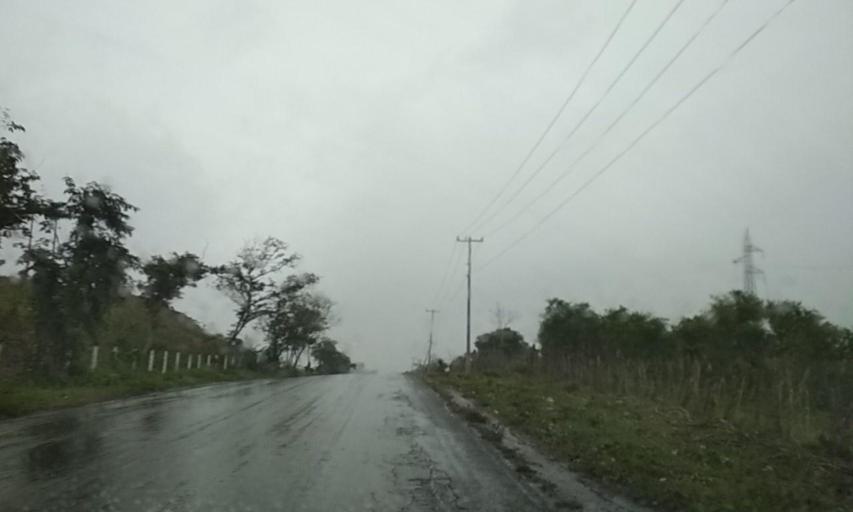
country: MX
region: Veracruz
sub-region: Papantla
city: El Chote
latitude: 20.3945
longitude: -97.3297
